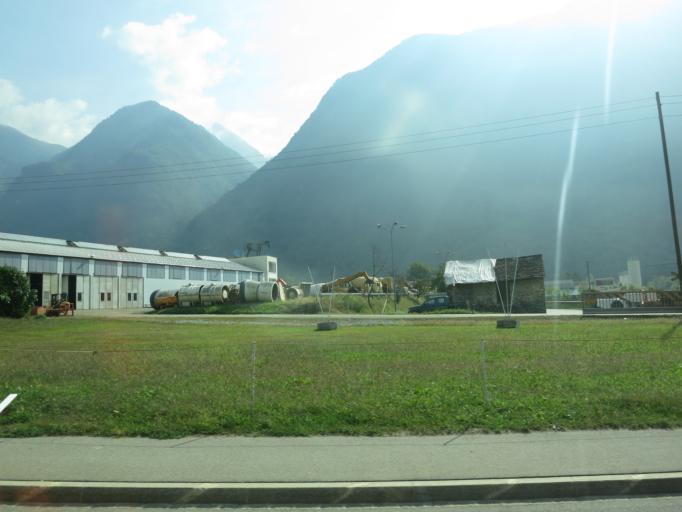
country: CH
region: Grisons
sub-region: Moesa District
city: Roveredo
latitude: 46.2420
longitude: 9.1386
